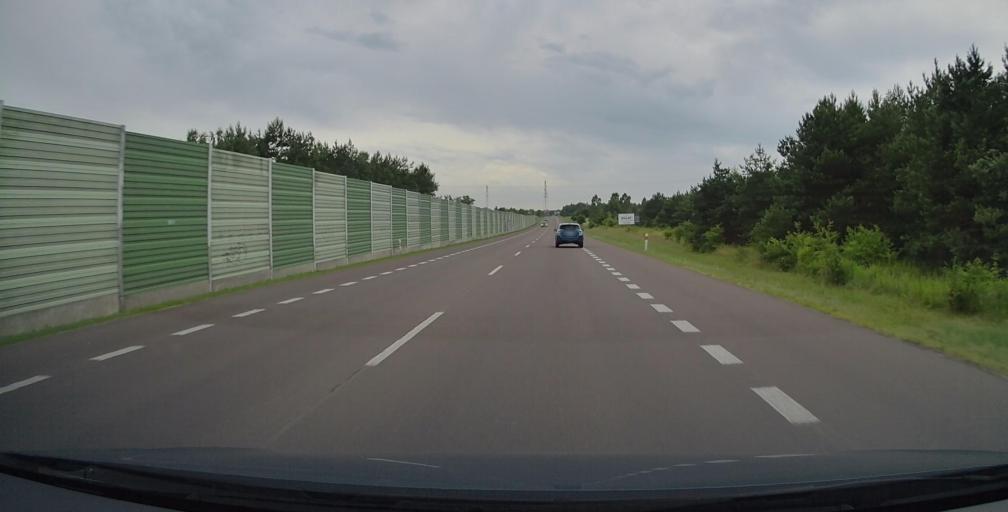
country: PL
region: Lublin Voivodeship
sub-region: Biala Podlaska
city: Biala Podlaska
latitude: 52.0417
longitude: 23.0875
